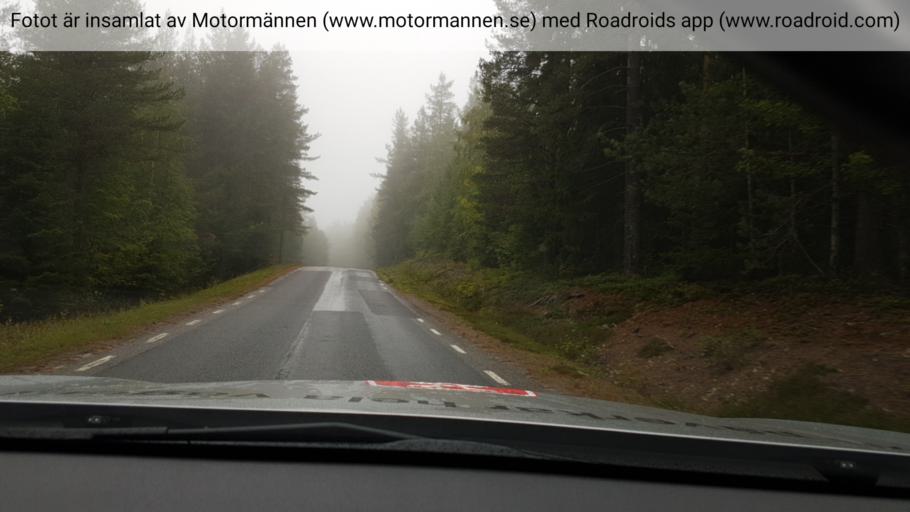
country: SE
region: Vaesterbotten
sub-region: Vannas Kommun
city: Vannasby
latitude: 64.0801
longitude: 20.0511
